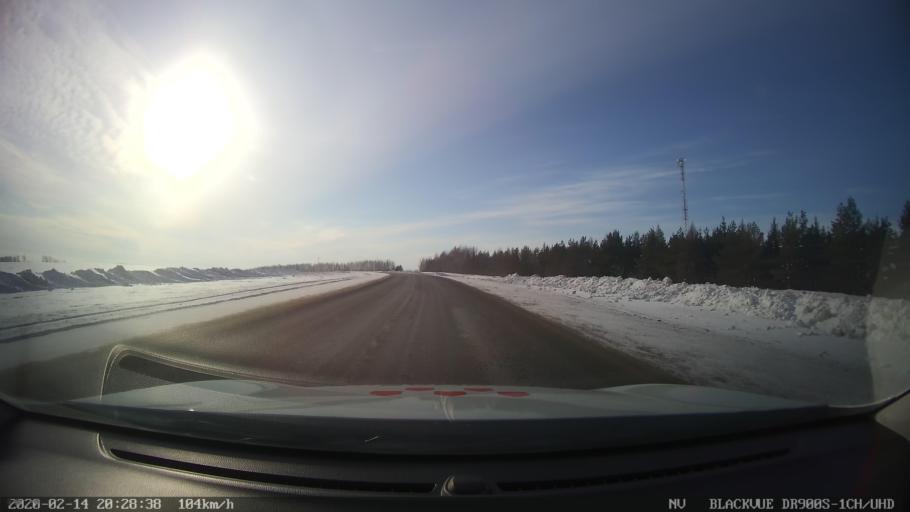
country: RU
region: Tatarstan
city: Stolbishchi
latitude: 55.4605
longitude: 48.9776
